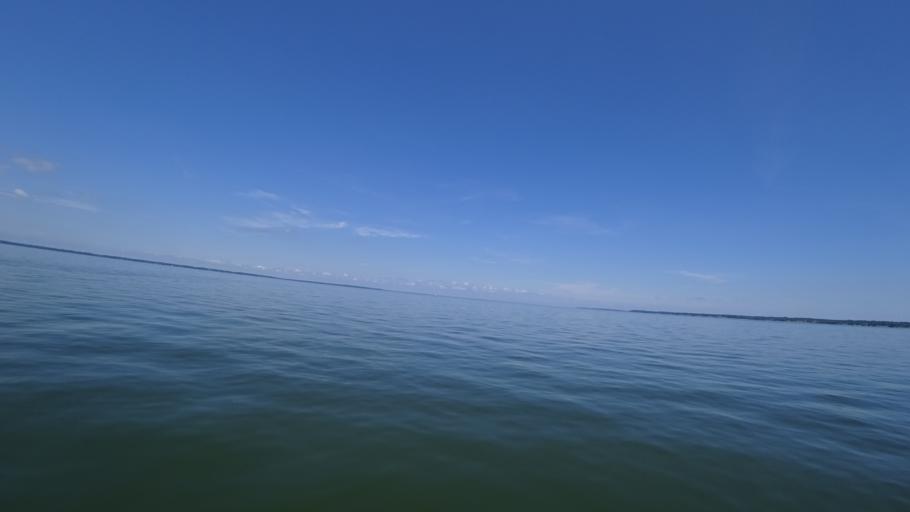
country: US
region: Virginia
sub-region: City of Newport News
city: Newport News
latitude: 37.0044
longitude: -76.4711
